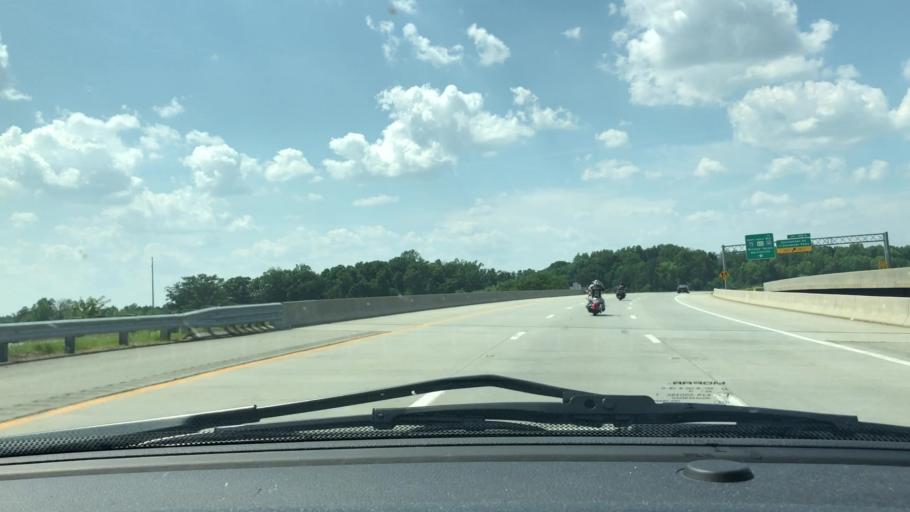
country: US
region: North Carolina
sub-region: Guilford County
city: Jamestown
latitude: 36.0051
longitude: -79.8496
